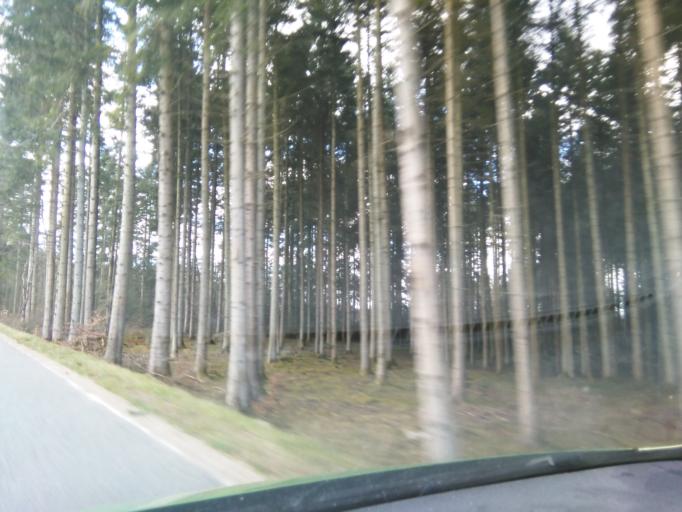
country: DK
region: Central Jutland
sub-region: Silkeborg Kommune
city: Virklund
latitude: 56.0513
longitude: 9.5771
